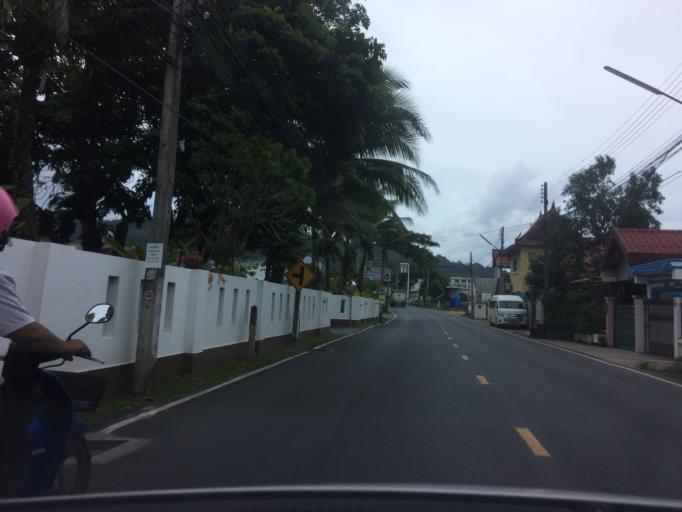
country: TH
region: Phuket
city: Mueang Phuket
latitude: 7.8646
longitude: 98.3581
